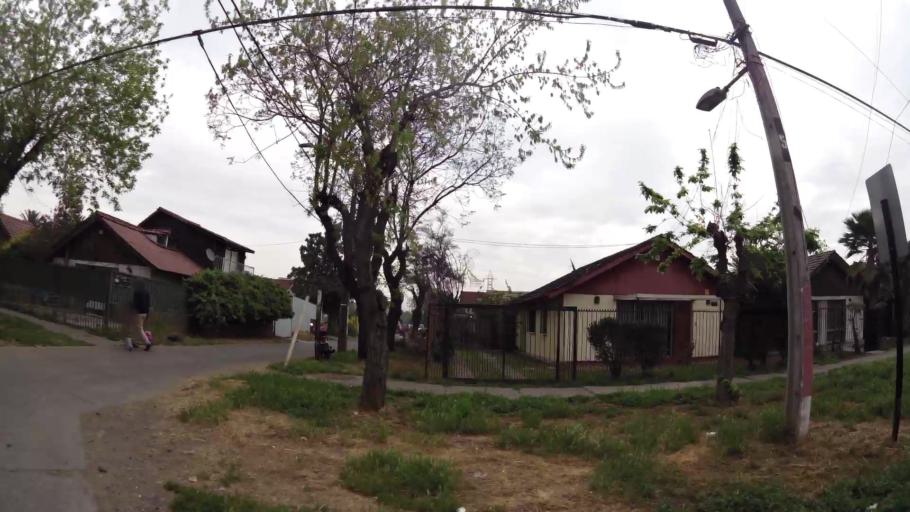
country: CL
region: Santiago Metropolitan
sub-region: Provincia de Santiago
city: Villa Presidente Frei, Nunoa, Santiago, Chile
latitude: -33.4750
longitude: -70.6074
